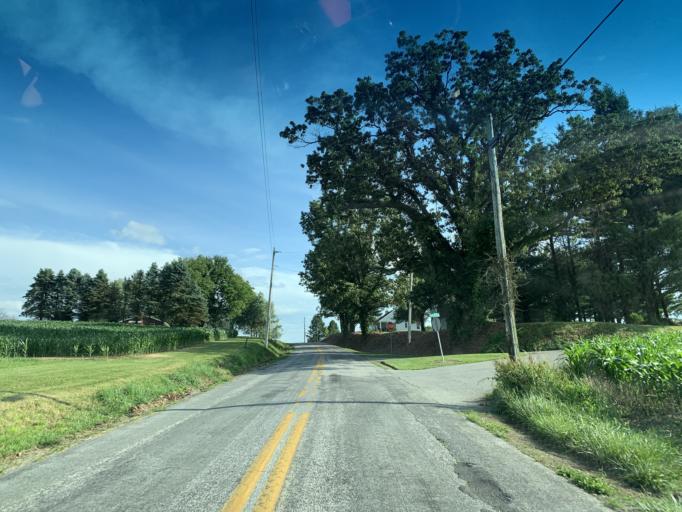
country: US
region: Pennsylvania
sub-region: York County
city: Stewartstown
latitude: 39.7289
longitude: -76.5430
